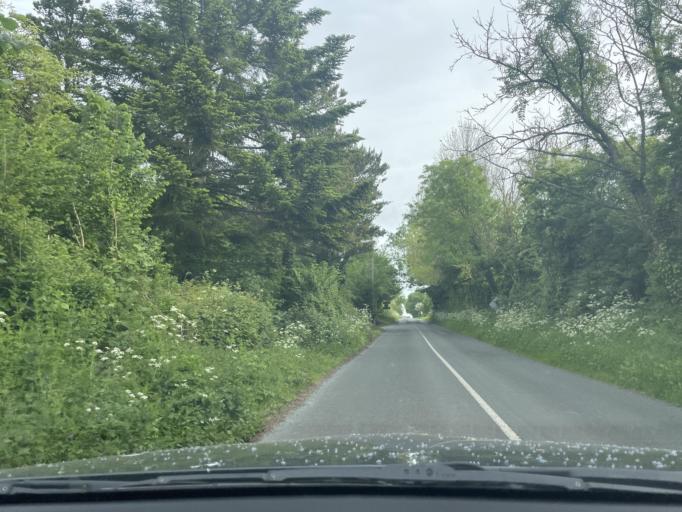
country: IE
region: Leinster
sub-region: County Carlow
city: Bagenalstown
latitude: 52.6558
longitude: -6.9637
